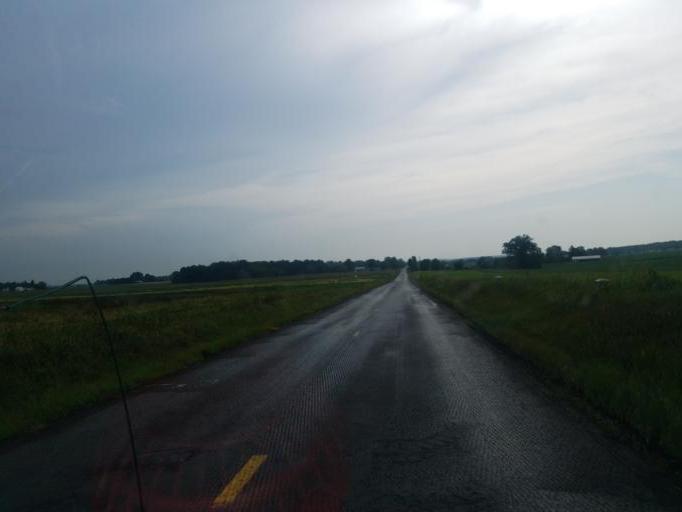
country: US
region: Ohio
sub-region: Wayne County
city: West Salem
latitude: 40.9242
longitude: -82.0673
